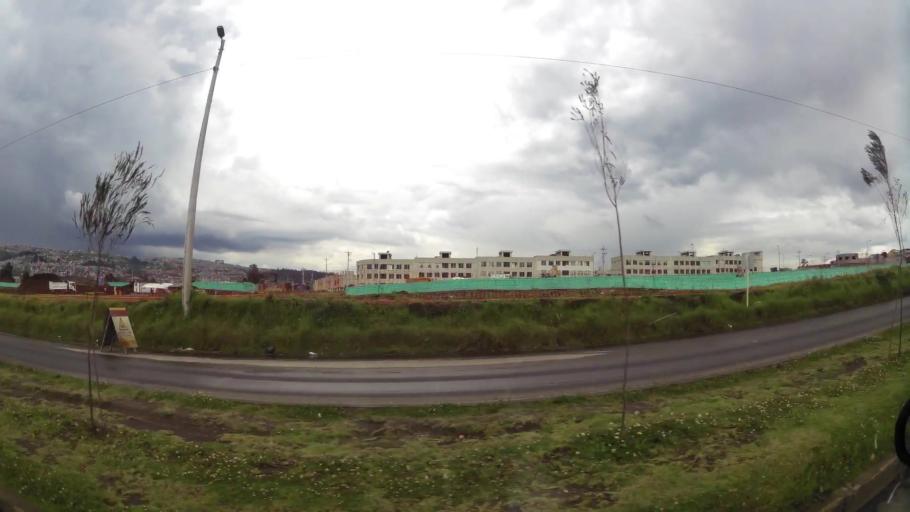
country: EC
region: Pichincha
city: Quito
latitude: -0.2990
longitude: -78.5549
